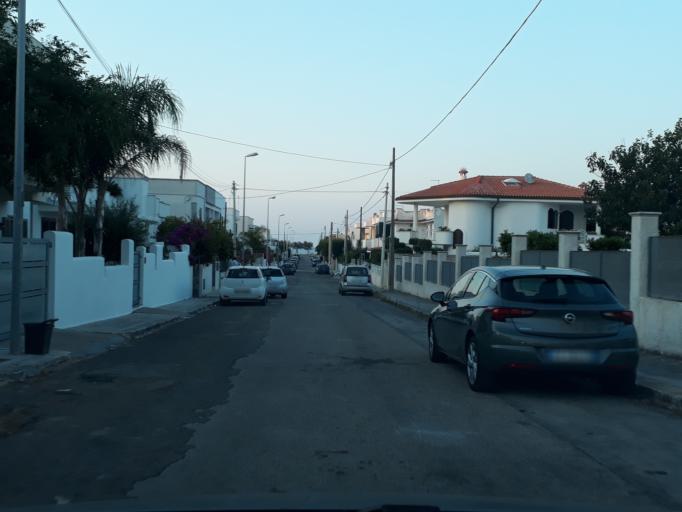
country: IT
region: Apulia
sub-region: Provincia di Brindisi
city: Carovigno
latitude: 40.7544
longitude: 17.7072
